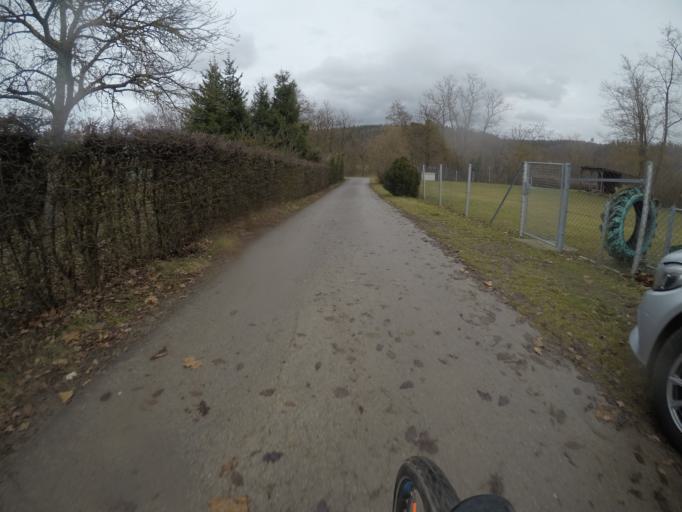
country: DE
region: Baden-Wuerttemberg
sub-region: Regierungsbezirk Stuttgart
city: Nufringen
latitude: 48.6133
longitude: 8.8803
